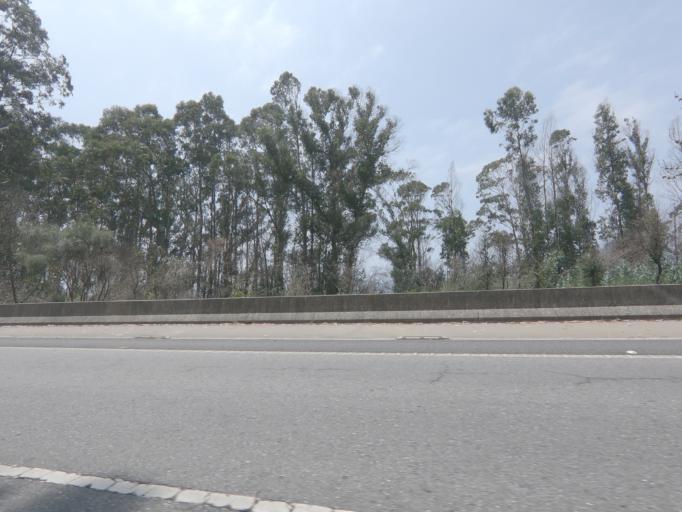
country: ES
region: Galicia
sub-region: Provincia de Pontevedra
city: A Guarda
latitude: 41.9264
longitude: -8.8812
